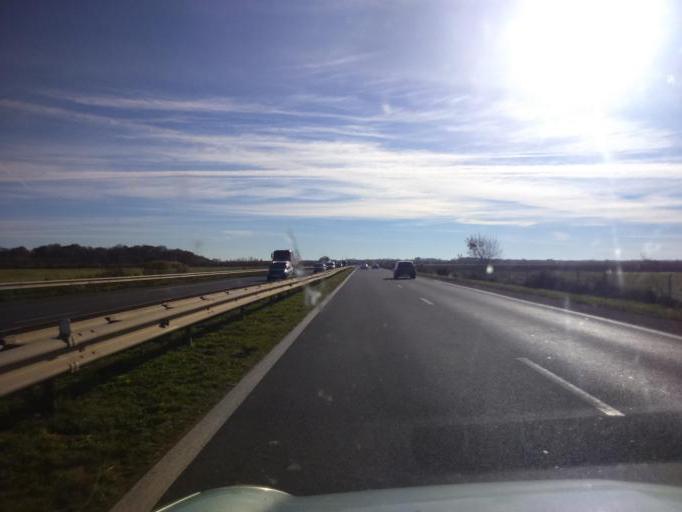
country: FR
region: Poitou-Charentes
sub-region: Departement de la Charente-Maritime
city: Saint-Laurent-de-la-Pree
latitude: 45.9829
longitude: -1.0193
